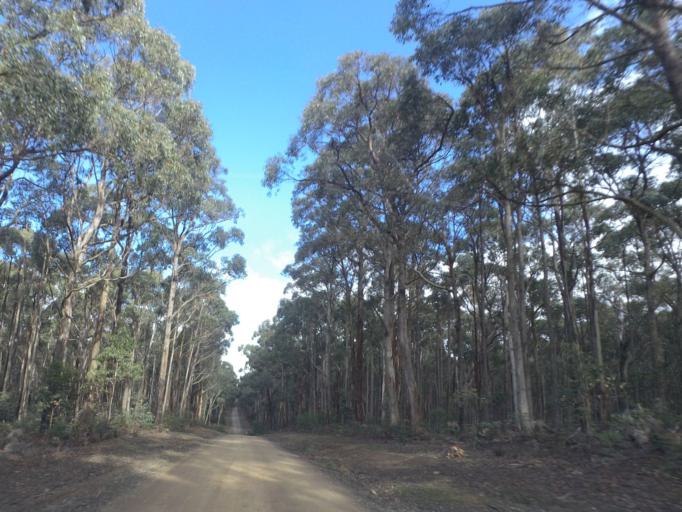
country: AU
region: Victoria
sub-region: Moorabool
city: Bacchus Marsh
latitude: -37.4405
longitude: 144.4566
